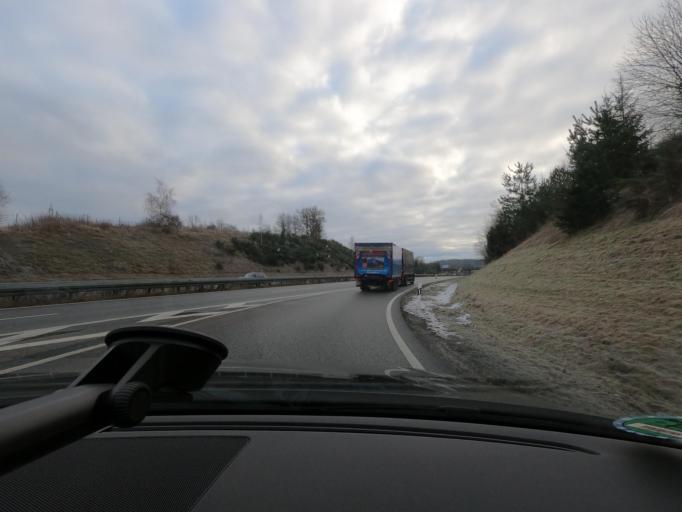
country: DE
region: Thuringia
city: Sankt Kilian
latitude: 50.5172
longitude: 10.7669
